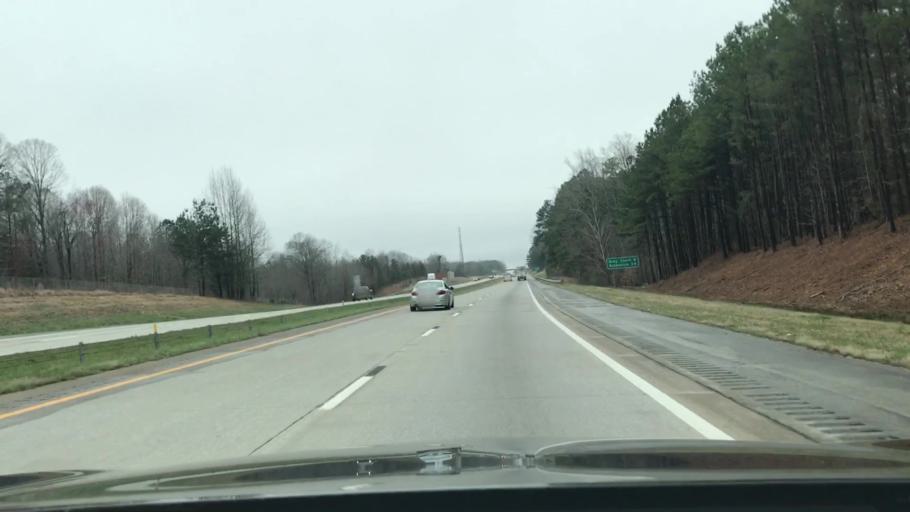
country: US
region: South Carolina
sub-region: Laurens County
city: Watts Mills
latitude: 34.5582
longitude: -82.0191
